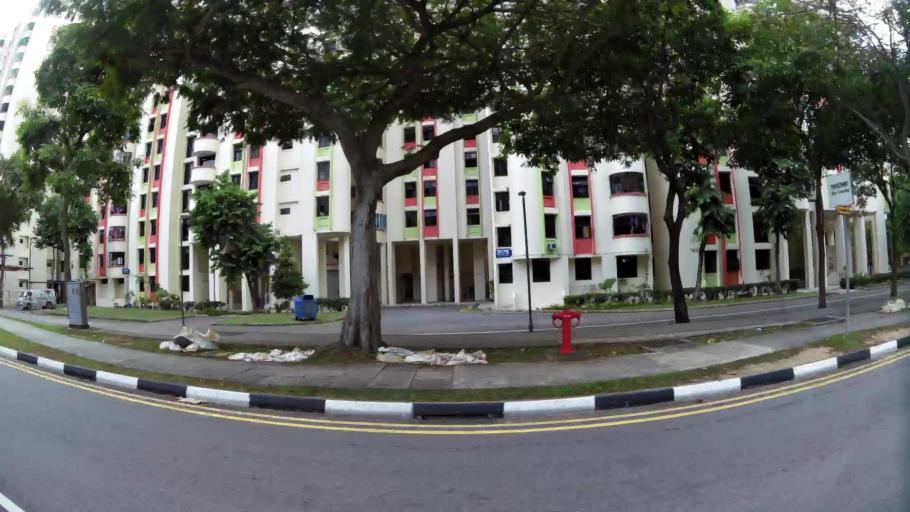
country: MY
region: Johor
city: Johor Bahru
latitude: 1.4502
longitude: 103.8178
